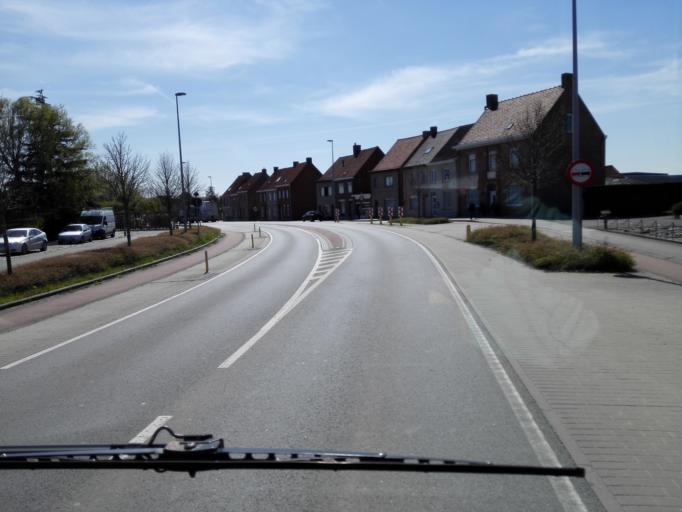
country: BE
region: Flanders
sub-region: Provincie West-Vlaanderen
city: Ingelmunster
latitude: 50.9306
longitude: 3.2611
